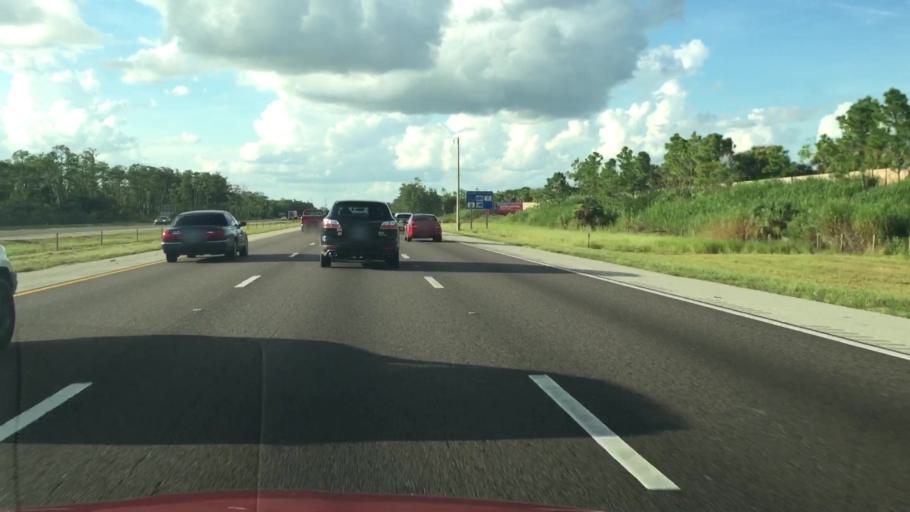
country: US
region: Florida
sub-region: Lee County
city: Gateway
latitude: 26.5944
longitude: -81.7969
